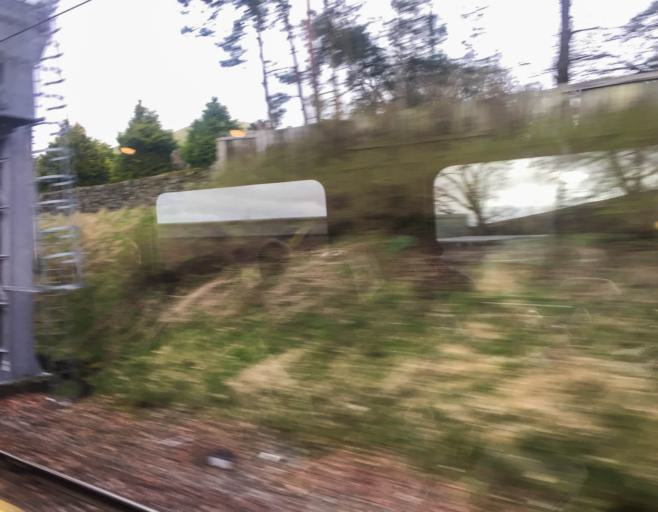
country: GB
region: Scotland
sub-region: South Lanarkshire
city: Douglas
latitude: 55.4926
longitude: -3.6860
